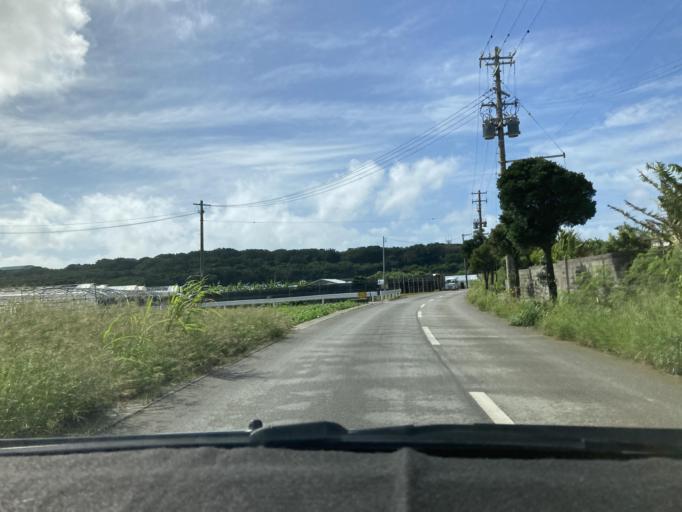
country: JP
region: Okinawa
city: Itoman
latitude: 26.1000
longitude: 127.6616
